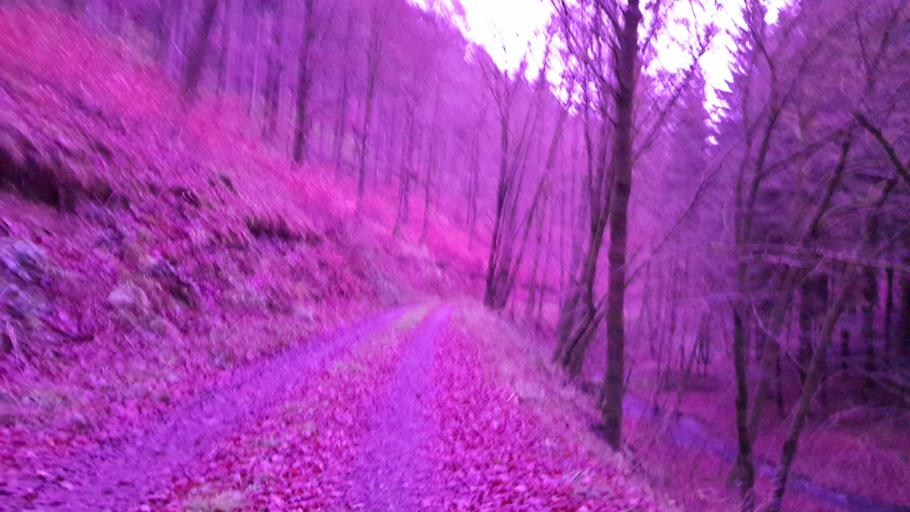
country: DE
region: Rheinland-Pfalz
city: Dasburg
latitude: 50.0787
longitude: 6.1037
